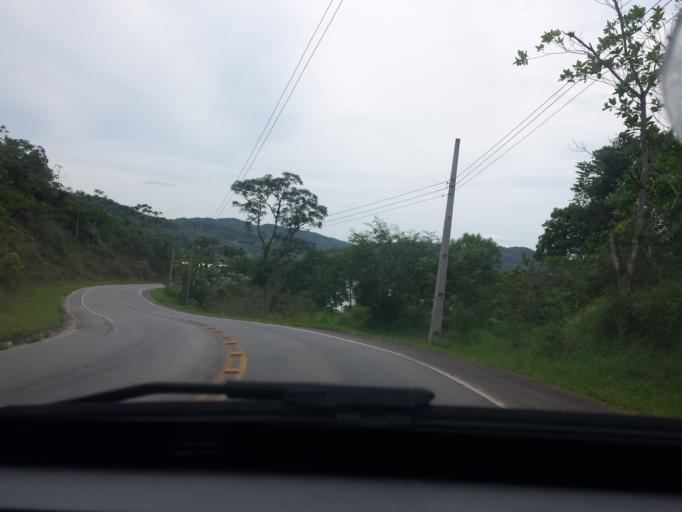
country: BR
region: Santa Catarina
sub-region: Blumenau
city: Blumenau
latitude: -26.8930
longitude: -49.0127
